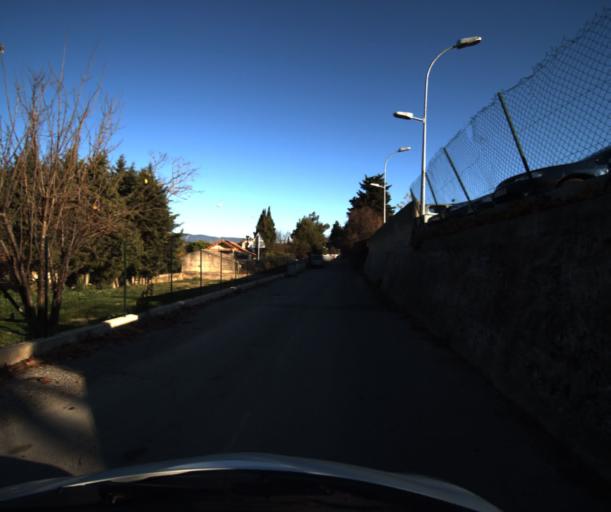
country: FR
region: Provence-Alpes-Cote d'Azur
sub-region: Departement du Vaucluse
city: Pertuis
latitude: 43.6954
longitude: 5.5080
